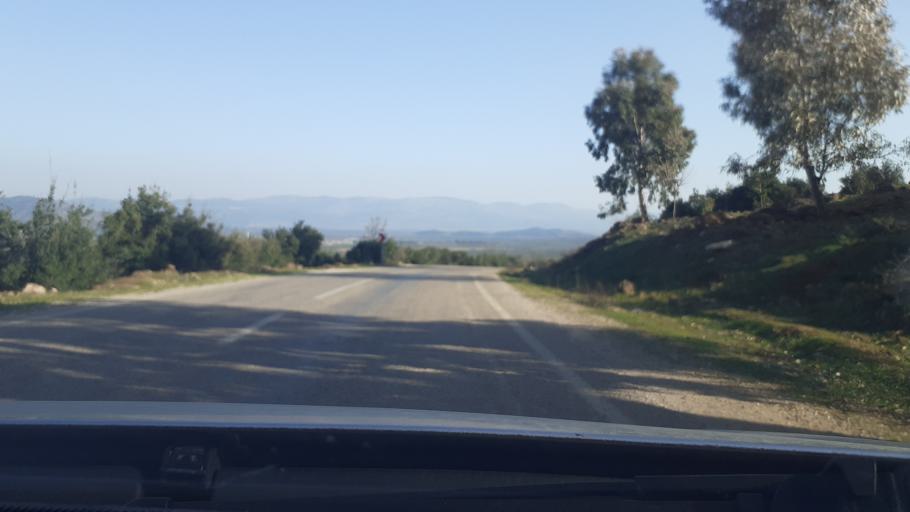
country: TR
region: Hatay
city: Aktepe
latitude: 36.7295
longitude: 36.4818
